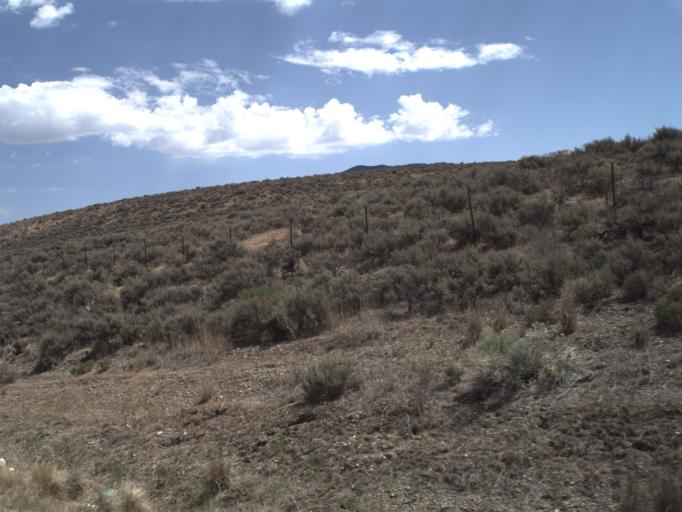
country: US
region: Utah
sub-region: Tooele County
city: Tooele
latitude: 40.4172
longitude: -112.3827
